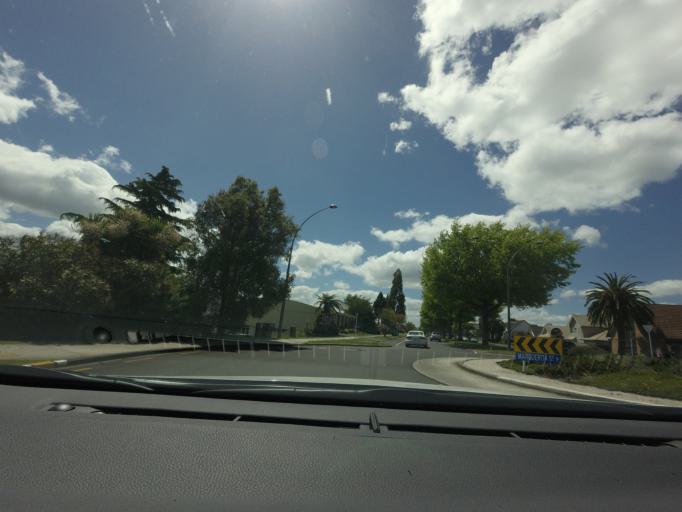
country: NZ
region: Bay of Plenty
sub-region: Rotorua District
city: Rotorua
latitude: -38.1512
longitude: 176.2537
